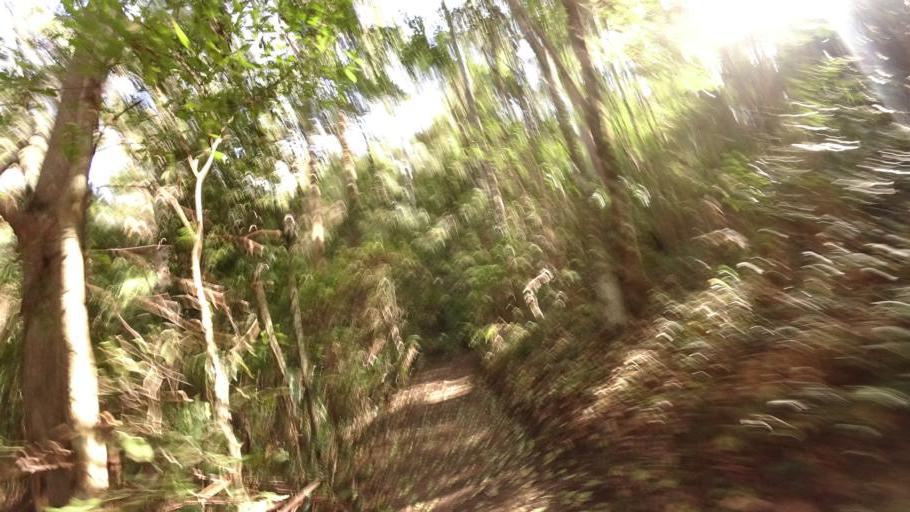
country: AU
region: Queensland
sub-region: Moreton Bay
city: Highvale
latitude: -27.4018
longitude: 152.8000
